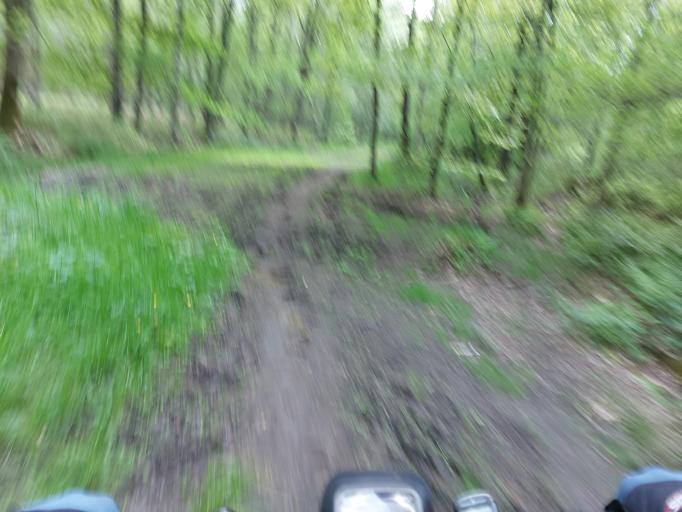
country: BE
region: Wallonia
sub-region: Province du Hainaut
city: Quaregnon
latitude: 50.5007
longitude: 3.8551
